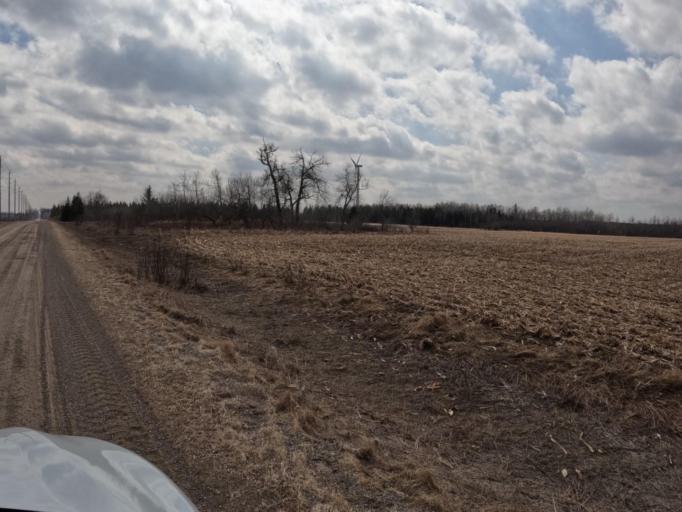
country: CA
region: Ontario
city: Shelburne
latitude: 44.0322
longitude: -80.3158
